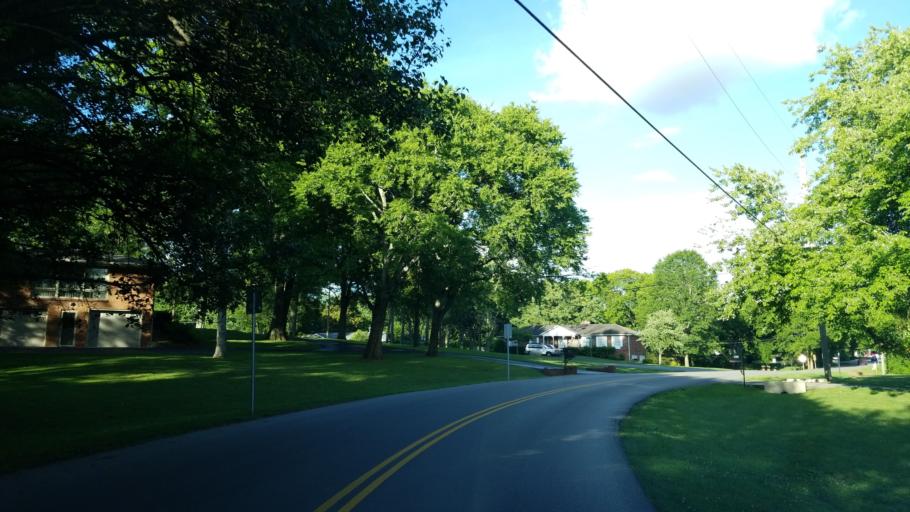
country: US
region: Tennessee
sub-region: Williamson County
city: Brentwood
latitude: 36.0296
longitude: -86.7962
